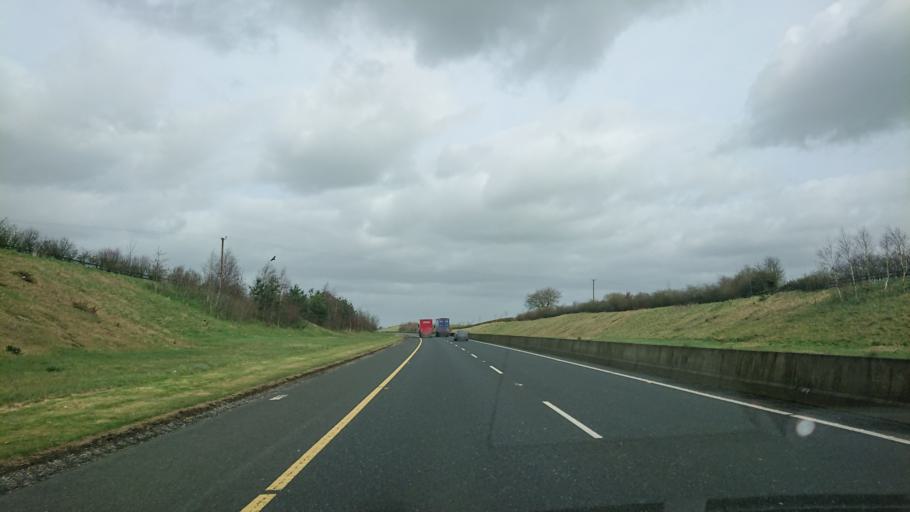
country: IE
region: Leinster
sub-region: Kildare
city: Old Kilcullen
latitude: 53.0658
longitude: -6.7652
